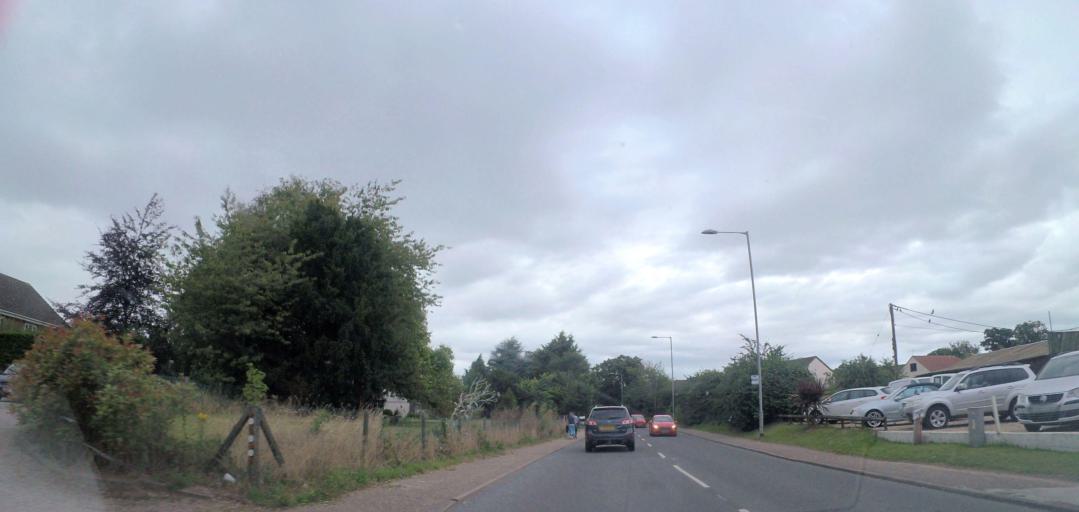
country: GB
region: England
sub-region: Norfolk
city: Coltishall
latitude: 52.7235
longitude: 1.3503
